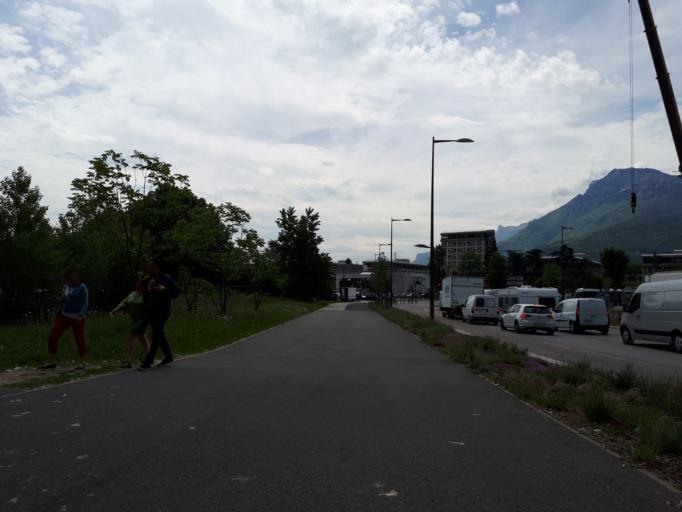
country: FR
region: Rhone-Alpes
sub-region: Departement de l'Isere
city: Saint-Martin-le-Vinoux
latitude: 45.2060
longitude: 5.7014
